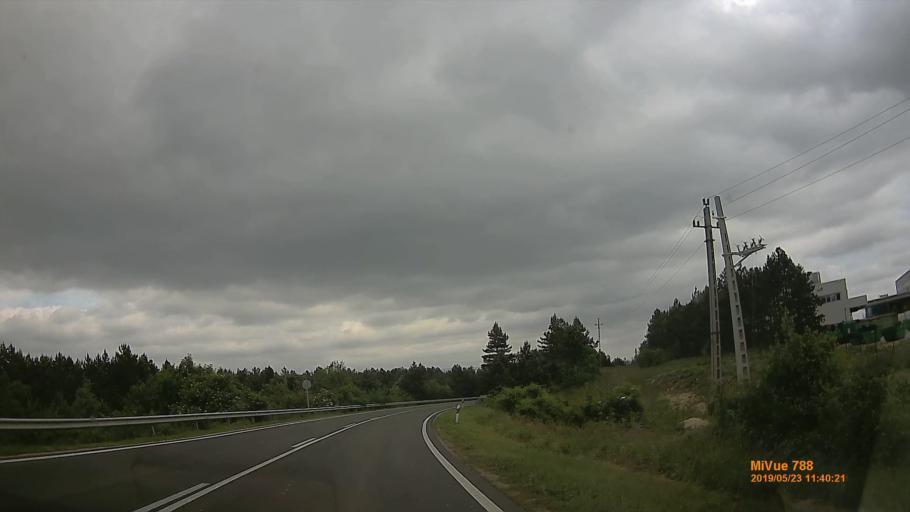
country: HU
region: Veszprem
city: Veszprem
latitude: 47.1118
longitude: 17.8719
